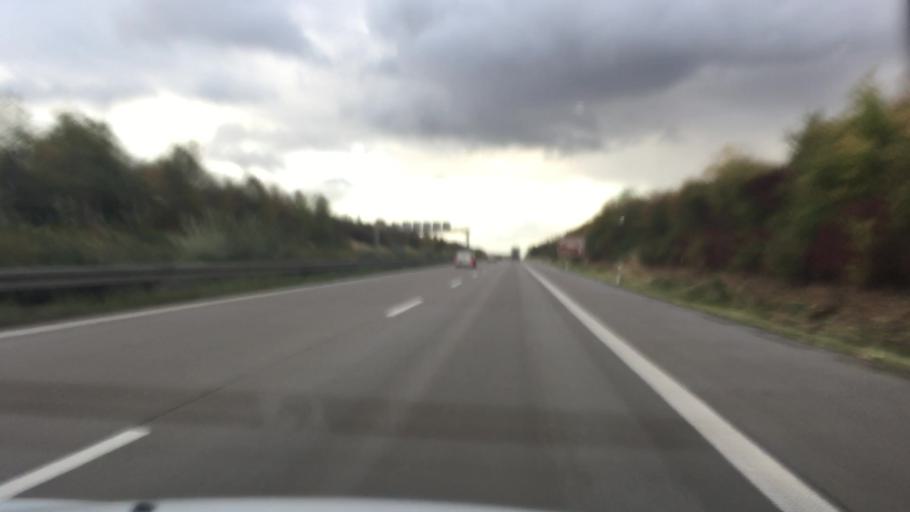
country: DE
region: Saxony-Anhalt
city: Welsleben
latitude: 52.0353
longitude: 11.6367
